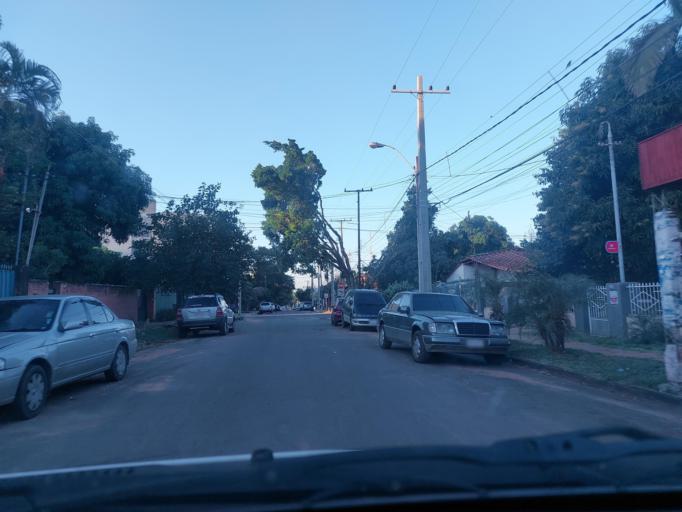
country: PY
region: Central
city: Fernando de la Mora
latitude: -25.3165
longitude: -57.5588
